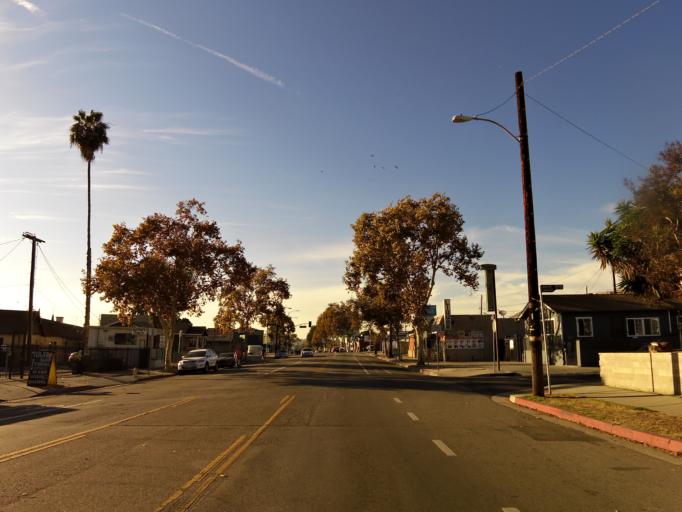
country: US
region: California
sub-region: Los Angeles County
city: South Pasadena
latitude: 34.1196
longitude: -118.1979
